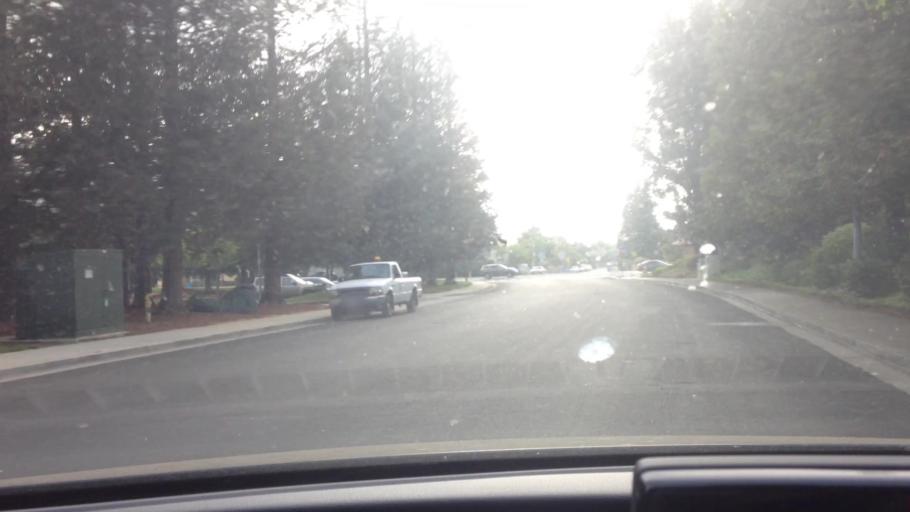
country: US
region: California
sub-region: Santa Clara County
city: Cupertino
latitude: 37.3252
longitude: -122.0429
